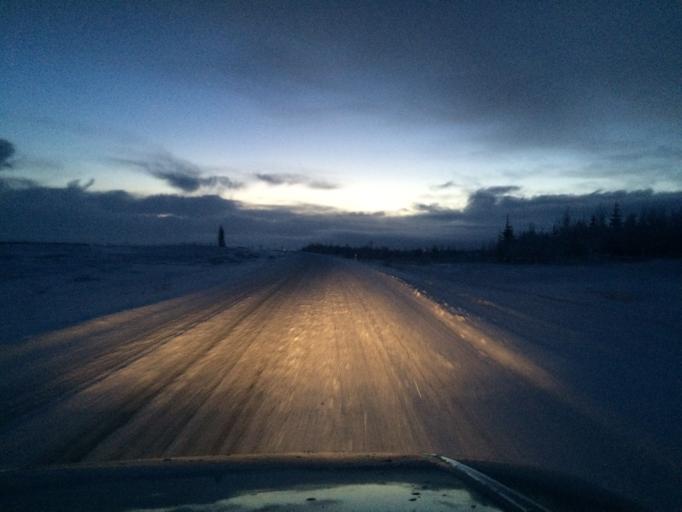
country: IS
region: South
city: Selfoss
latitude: 64.0836
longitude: -20.7479
